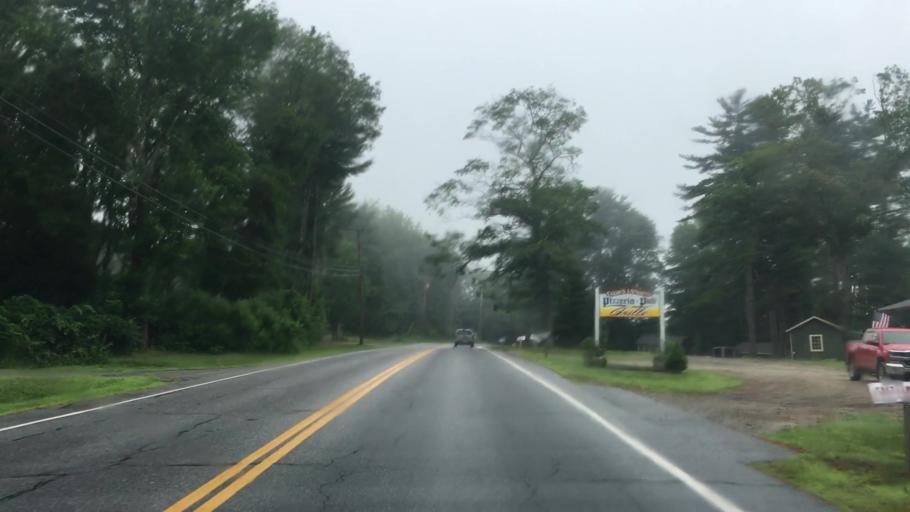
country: US
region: Maine
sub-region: Lincoln County
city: Edgecomb
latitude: 43.9638
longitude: -69.6295
